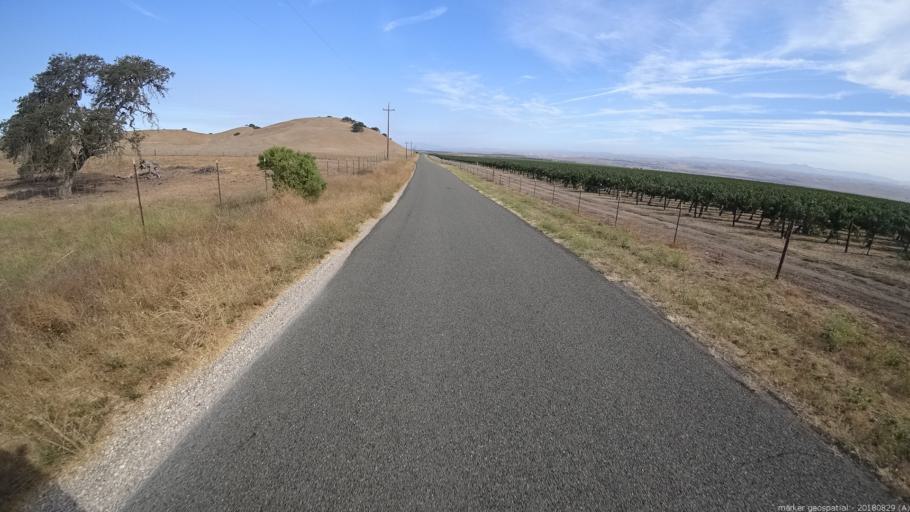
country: US
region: California
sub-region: Monterey County
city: King City
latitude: 36.0755
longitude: -121.0381
